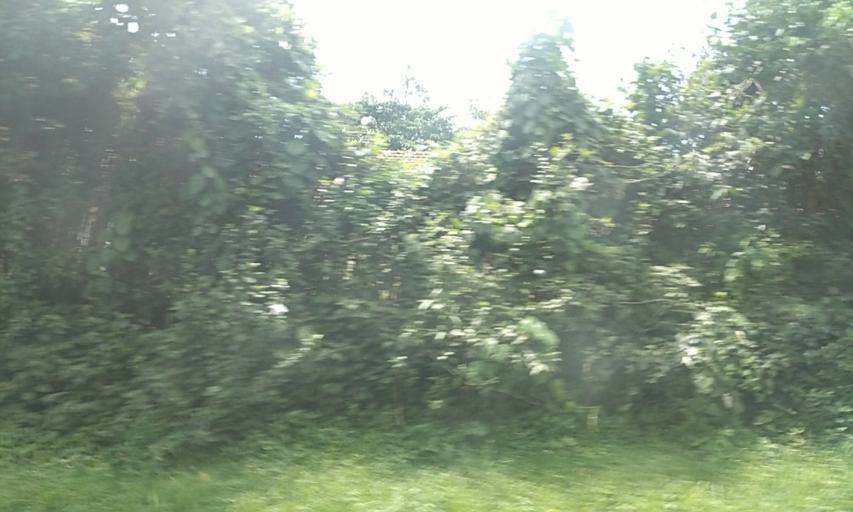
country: UG
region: Central Region
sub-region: Kampala District
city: Kampala
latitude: 0.3307
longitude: 32.6013
